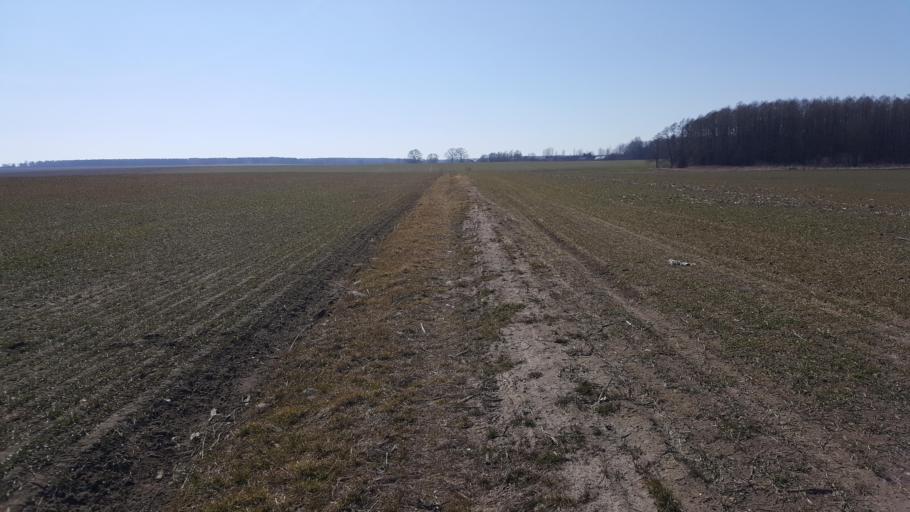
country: BY
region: Brest
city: Kamyanyets
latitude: 52.3680
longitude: 23.7734
